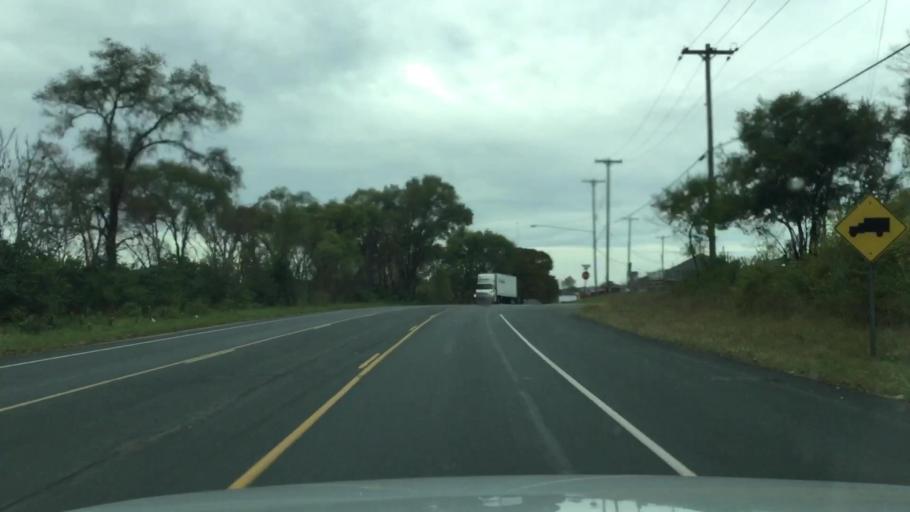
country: US
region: Michigan
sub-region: Kalamazoo County
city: Eastwood
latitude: 42.2884
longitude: -85.5509
